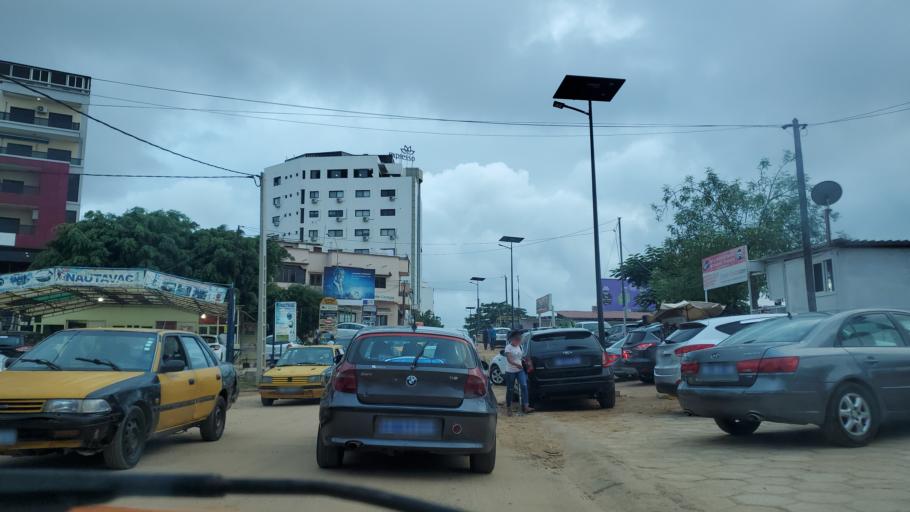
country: SN
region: Dakar
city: Mermoz Boabab
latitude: 14.7200
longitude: -17.4706
